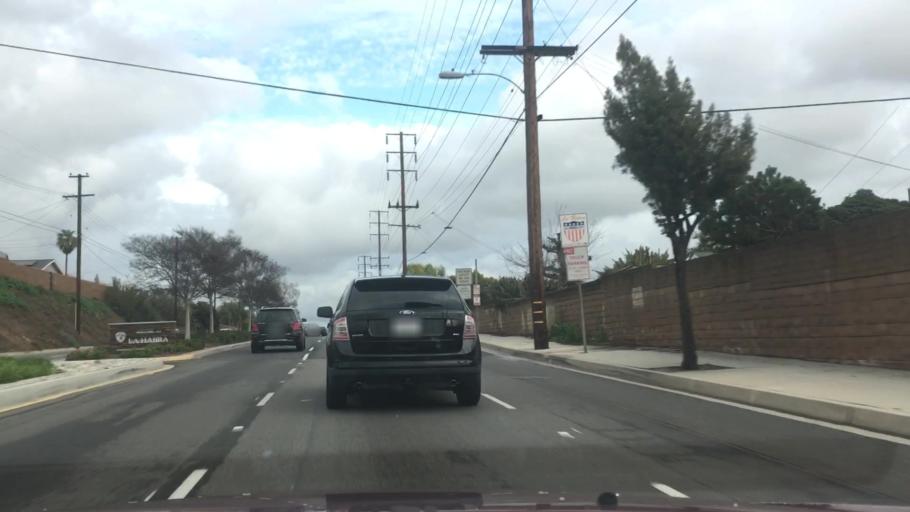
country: US
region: California
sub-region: Los Angeles County
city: East La Mirada
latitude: 33.9173
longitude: -117.9768
